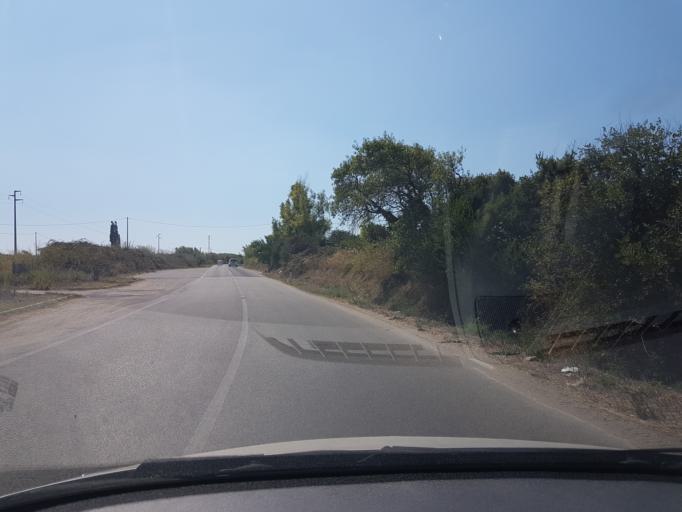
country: IT
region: Sardinia
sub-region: Provincia di Oristano
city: Riola Sardo
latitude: 40.0025
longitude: 8.5311
